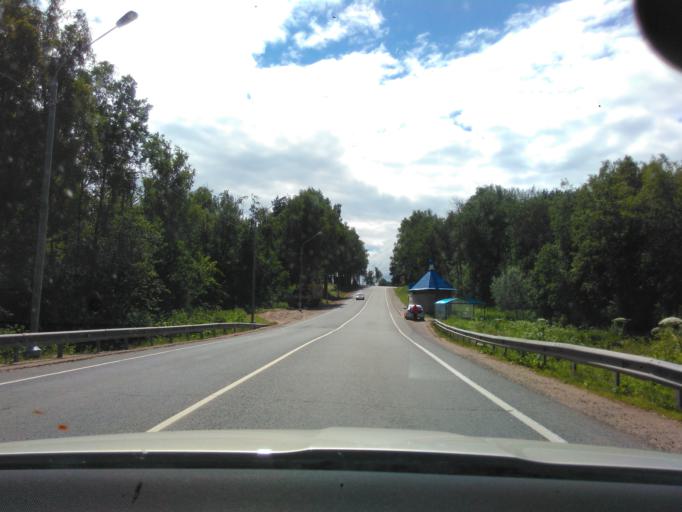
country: RU
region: Moskovskaya
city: Shevlyakovo
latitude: 56.3860
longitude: 36.8601
